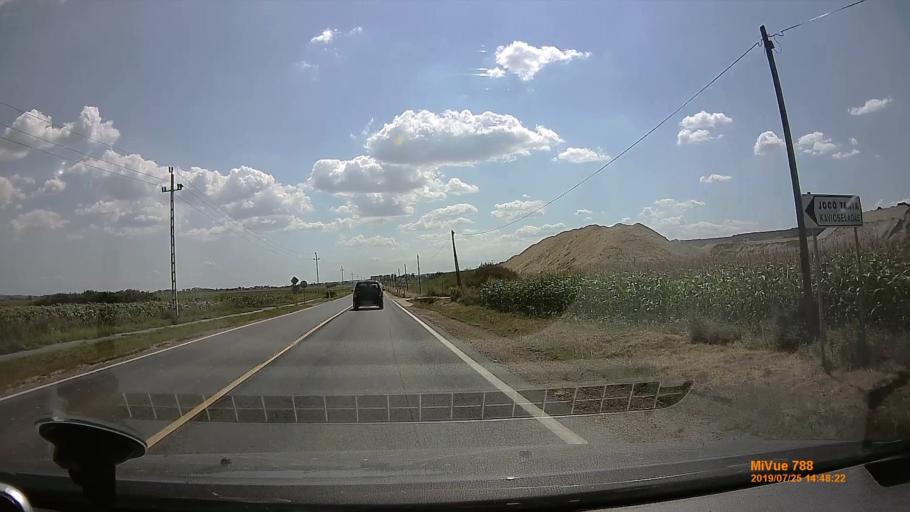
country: HU
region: Borsod-Abauj-Zemplen
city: Aszalo
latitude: 48.2381
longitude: 20.9665
